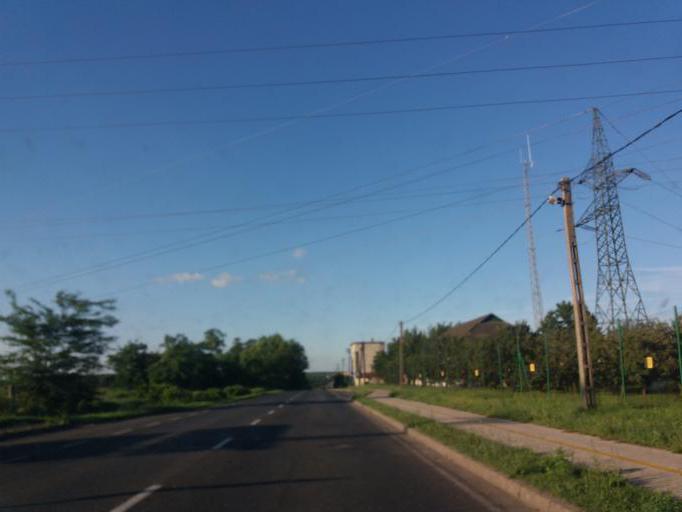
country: HU
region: Fejer
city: Baracska
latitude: 47.2803
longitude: 18.7498
